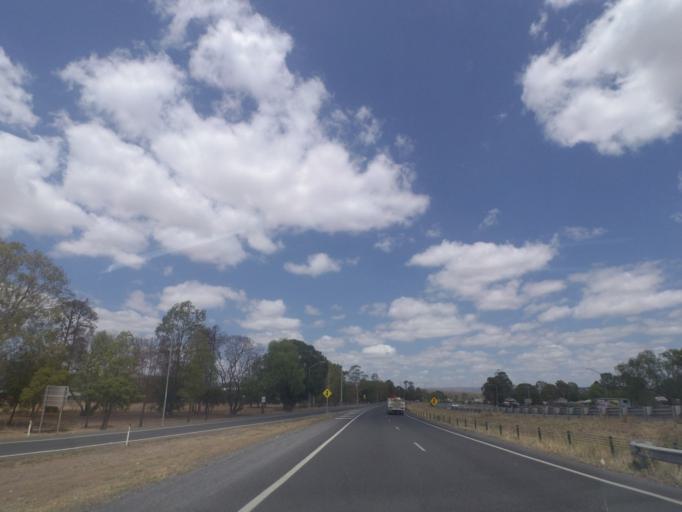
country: AU
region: Queensland
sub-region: Lockyer Valley
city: Gatton
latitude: -27.5531
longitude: 152.1275
